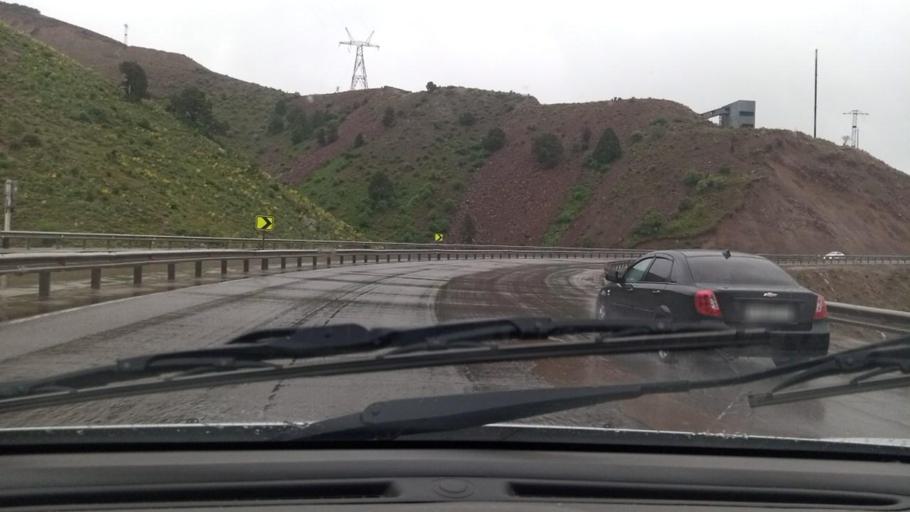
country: UZ
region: Toshkent
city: Angren
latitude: 41.0901
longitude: 70.5352
